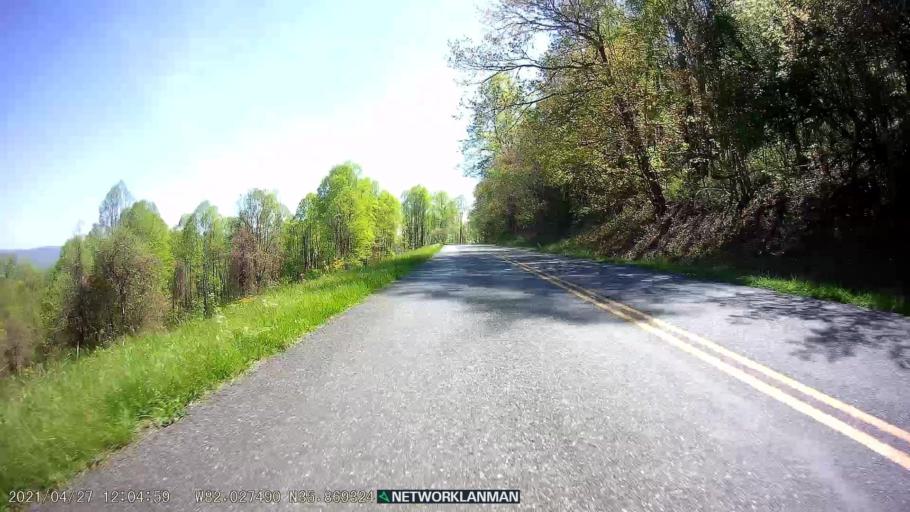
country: US
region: North Carolina
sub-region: Mitchell County
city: Spruce Pine
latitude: 35.8693
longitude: -82.0275
